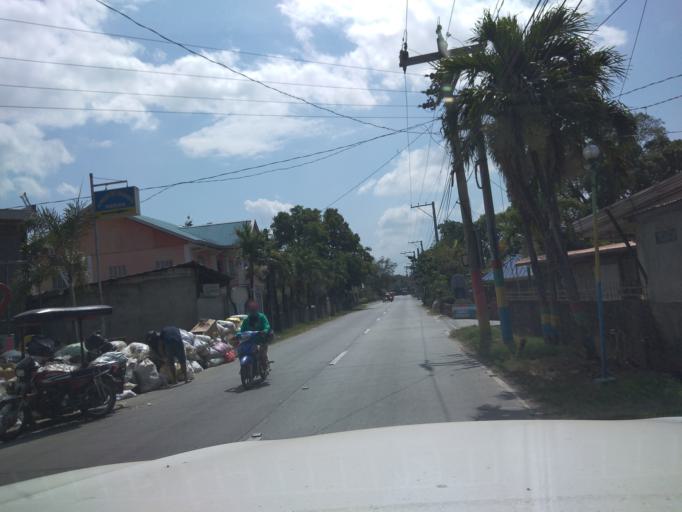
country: PH
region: Central Luzon
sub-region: Province of Pampanga
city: Lourdes
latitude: 15.0201
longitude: 120.8492
